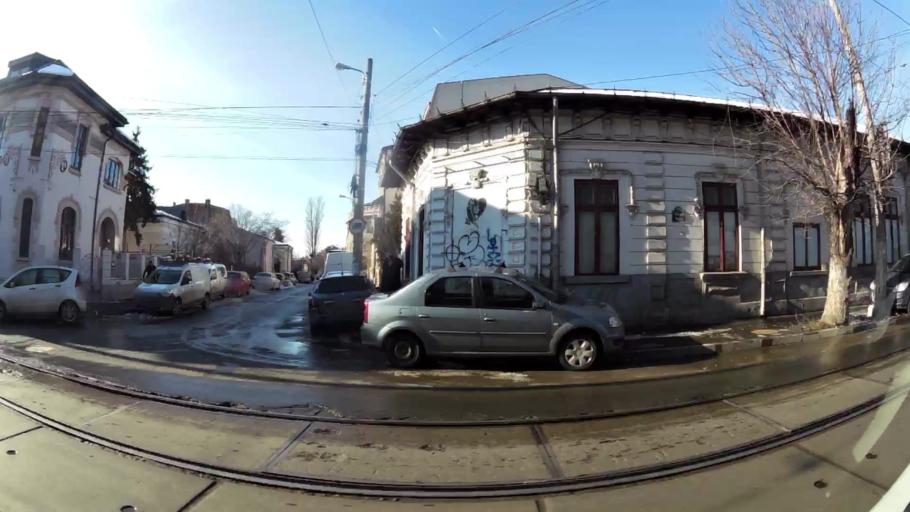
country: RO
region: Bucuresti
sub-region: Municipiul Bucuresti
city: Bucharest
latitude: 44.4347
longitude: 26.1211
